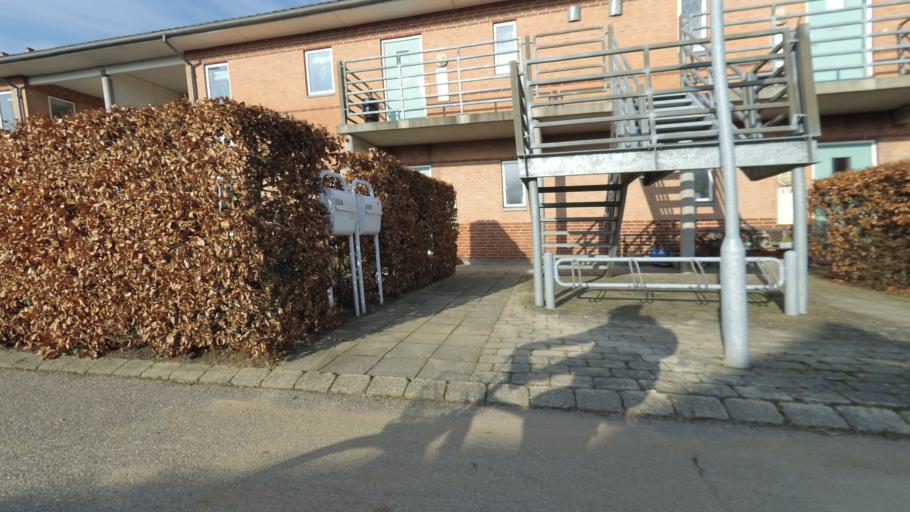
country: DK
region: Central Jutland
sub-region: Arhus Kommune
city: Kolt
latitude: 56.1105
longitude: 10.0789
